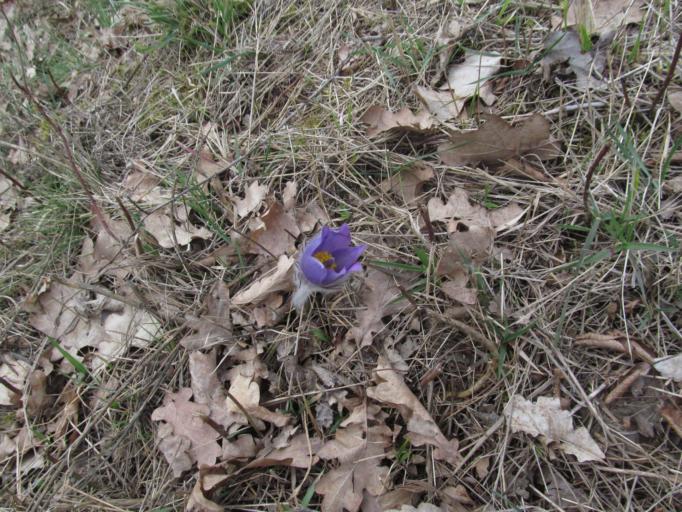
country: HU
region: Borsod-Abauj-Zemplen
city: Rudabanya
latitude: 48.4719
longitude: 20.4827
